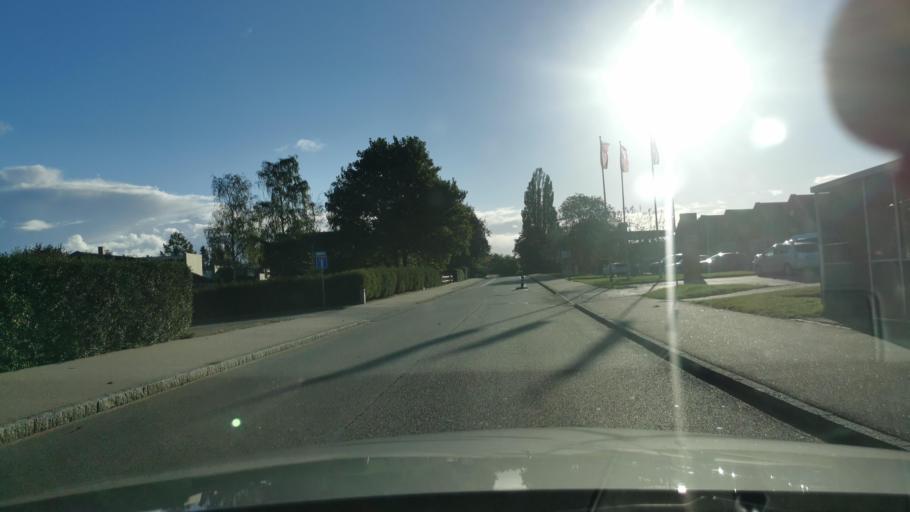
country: DK
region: Zealand
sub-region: Kalundborg Kommune
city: Svebolle
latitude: 55.6537
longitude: 11.2786
